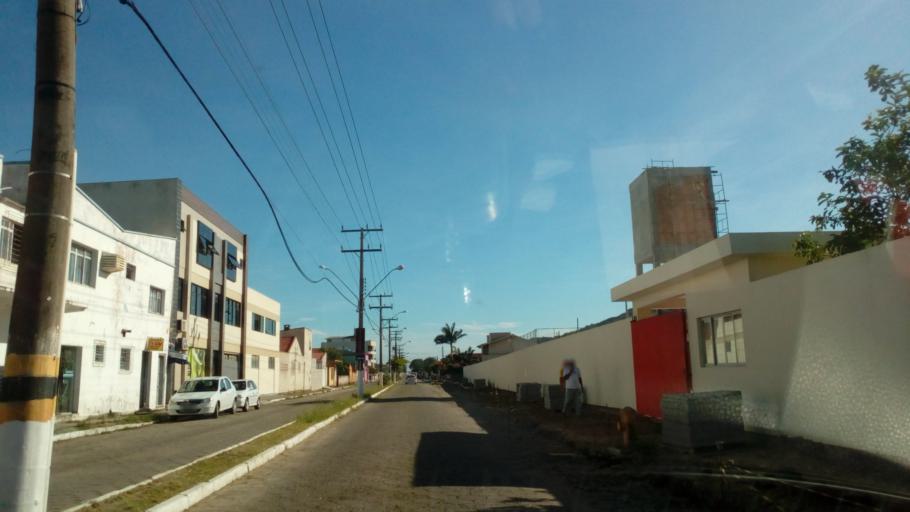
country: BR
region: Santa Catarina
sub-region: Laguna
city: Laguna
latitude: -28.4793
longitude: -48.7839
